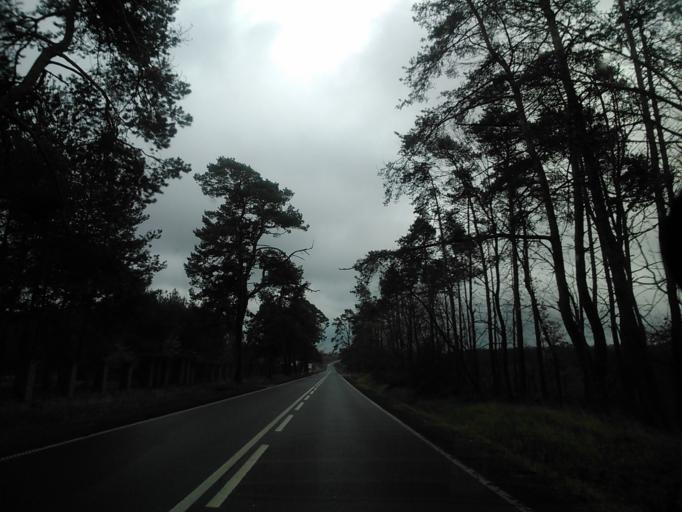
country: PL
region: Kujawsko-Pomorskie
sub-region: Powiat golubsko-dobrzynski
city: Golub-Dobrzyn
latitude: 53.1053
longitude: 19.1246
